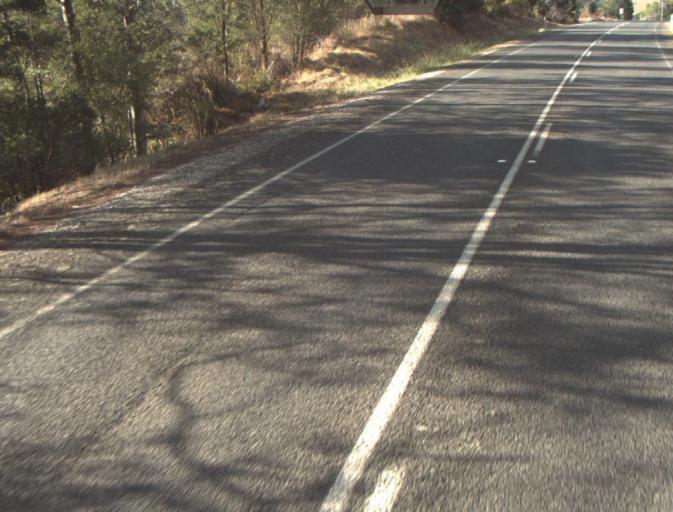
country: AU
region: Tasmania
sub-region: Launceston
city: Mayfield
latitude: -41.2651
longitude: 147.2155
